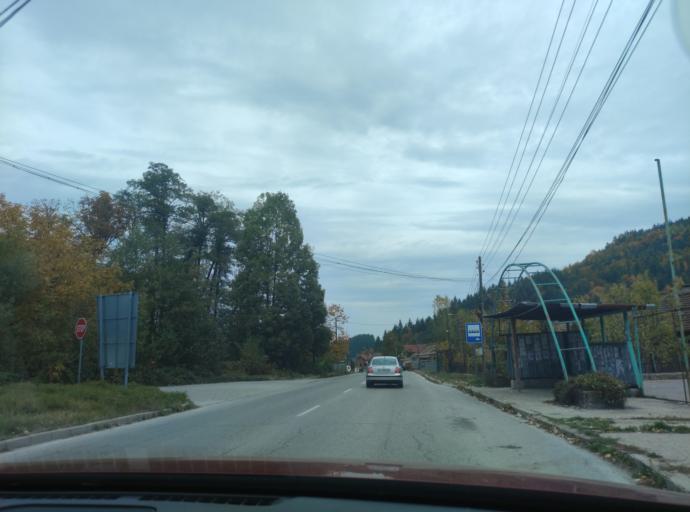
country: BG
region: Montana
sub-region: Obshtina Berkovitsa
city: Berkovitsa
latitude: 43.1900
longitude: 23.1590
